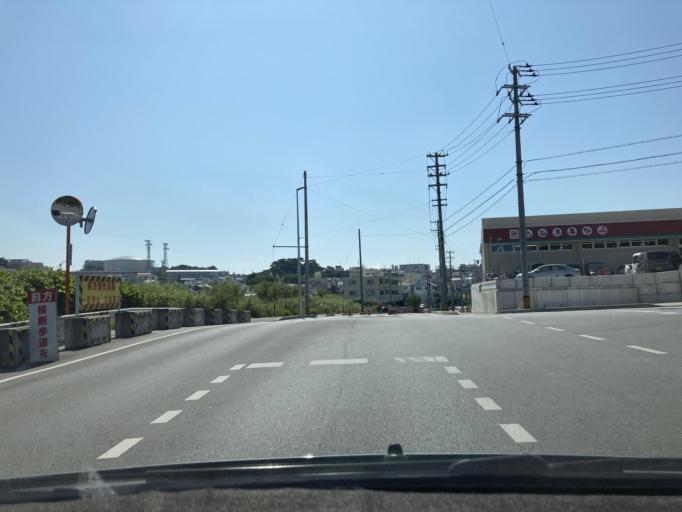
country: JP
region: Okinawa
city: Ginowan
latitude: 26.2414
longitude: 127.7258
